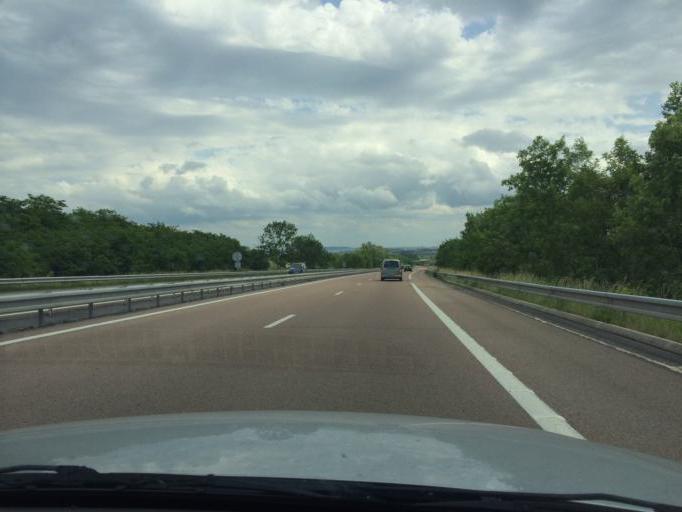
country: FR
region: Champagne-Ardenne
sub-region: Departement de la Marne
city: Gueux
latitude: 49.2431
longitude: 3.8966
